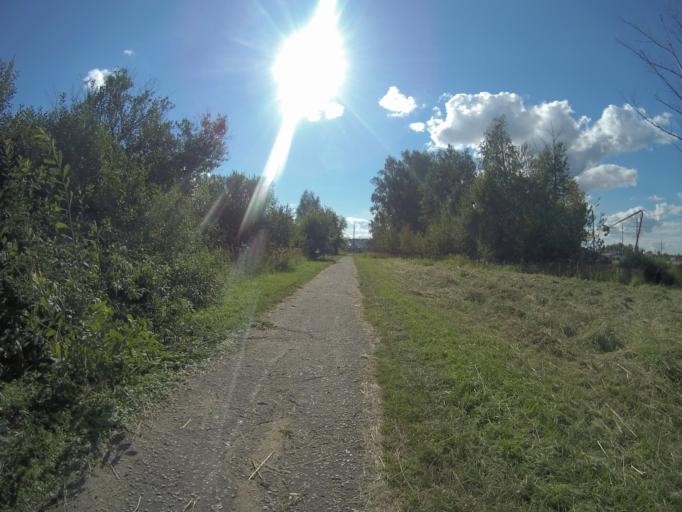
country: RU
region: Vladimir
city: Vladimir
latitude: 56.1718
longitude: 40.4250
